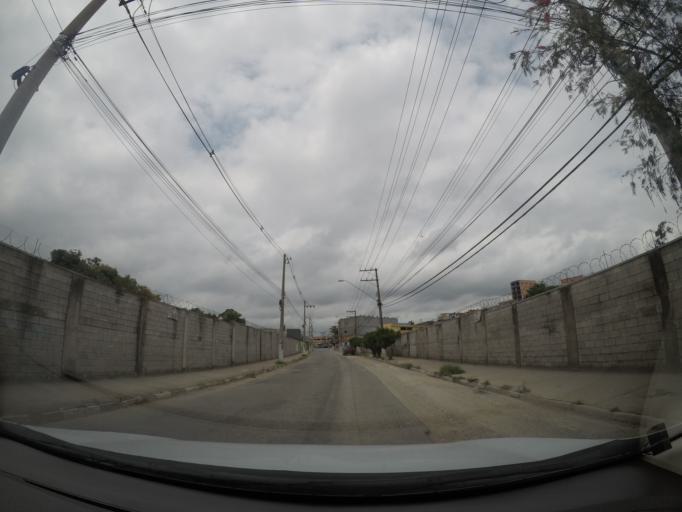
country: BR
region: Sao Paulo
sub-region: Itaquaquecetuba
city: Itaquaquecetuba
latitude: -23.4408
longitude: -46.3864
